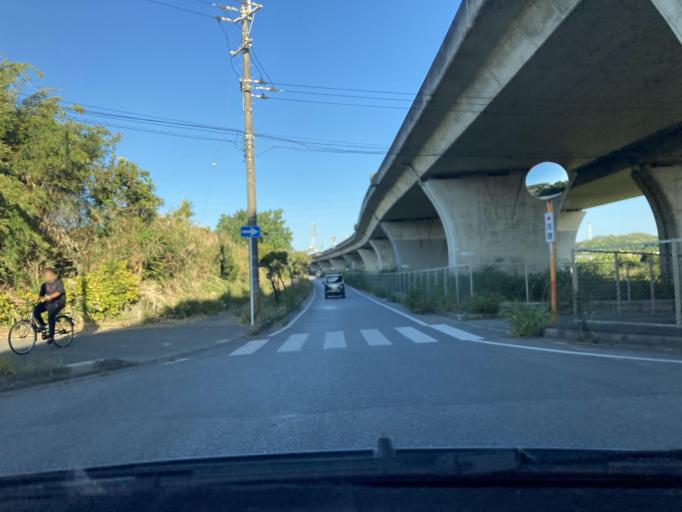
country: JP
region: Okinawa
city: Tomigusuku
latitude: 26.1812
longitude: 127.7285
